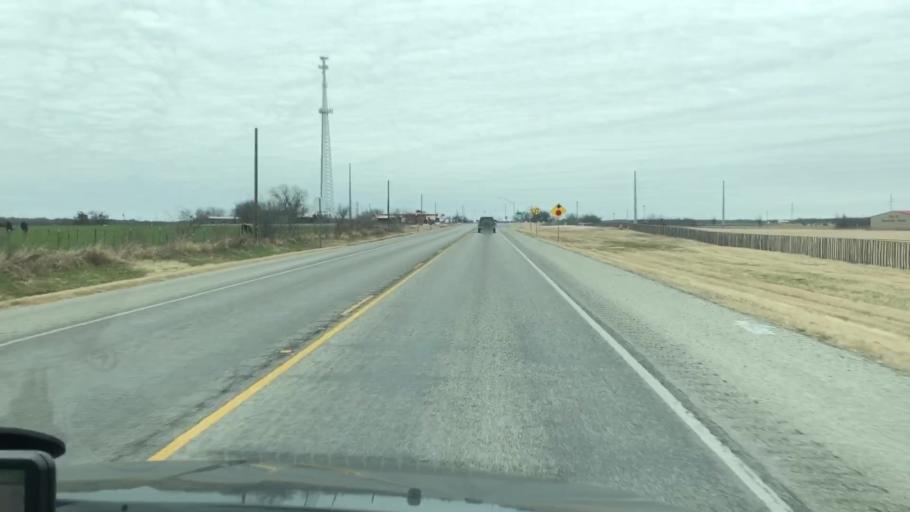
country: US
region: Texas
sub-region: Palo Pinto County
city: Mineral Wells
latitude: 32.9167
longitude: -98.0765
